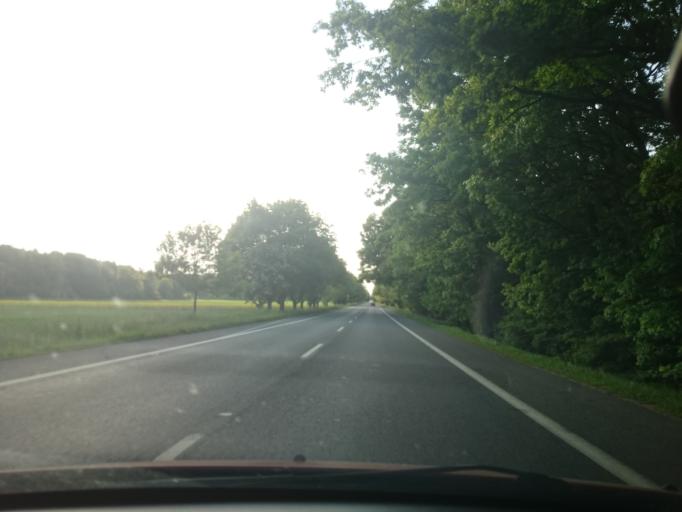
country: PL
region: Opole Voivodeship
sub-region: Powiat strzelecki
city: Strzelce Opolskie
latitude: 50.5378
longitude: 18.2502
